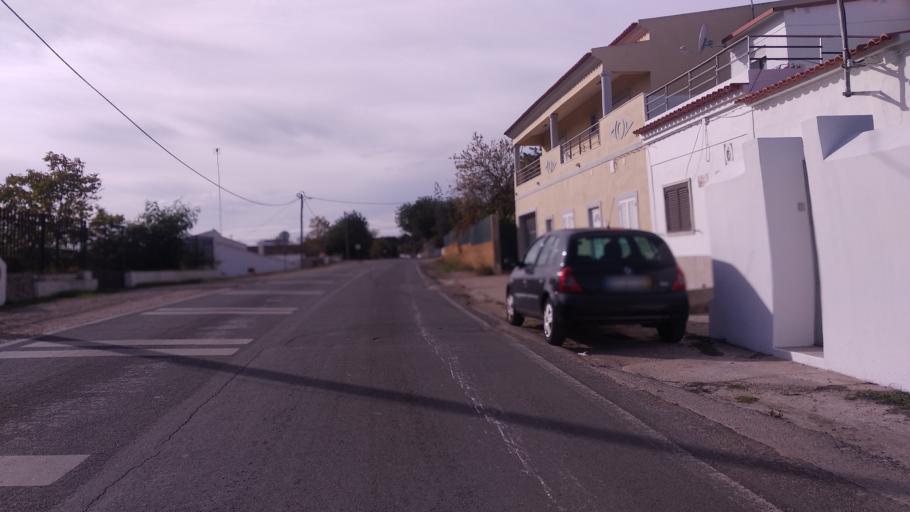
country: PT
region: Faro
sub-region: Sao Bras de Alportel
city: Sao Bras de Alportel
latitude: 37.1533
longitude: -7.8985
